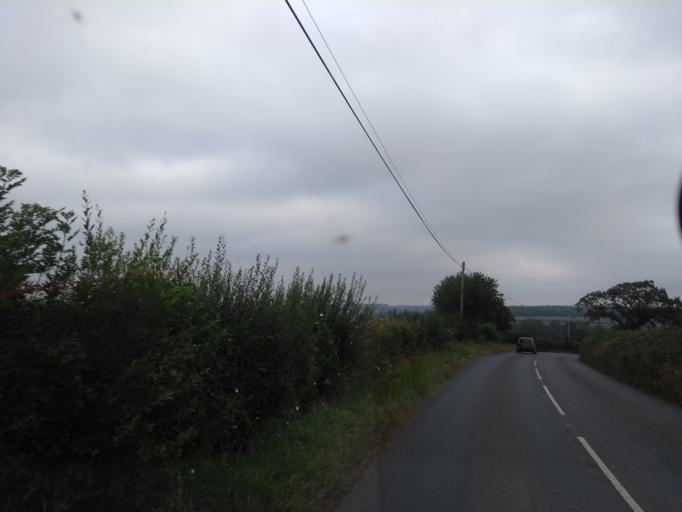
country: GB
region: England
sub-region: Somerset
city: Chard
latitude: 50.8903
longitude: -3.0882
